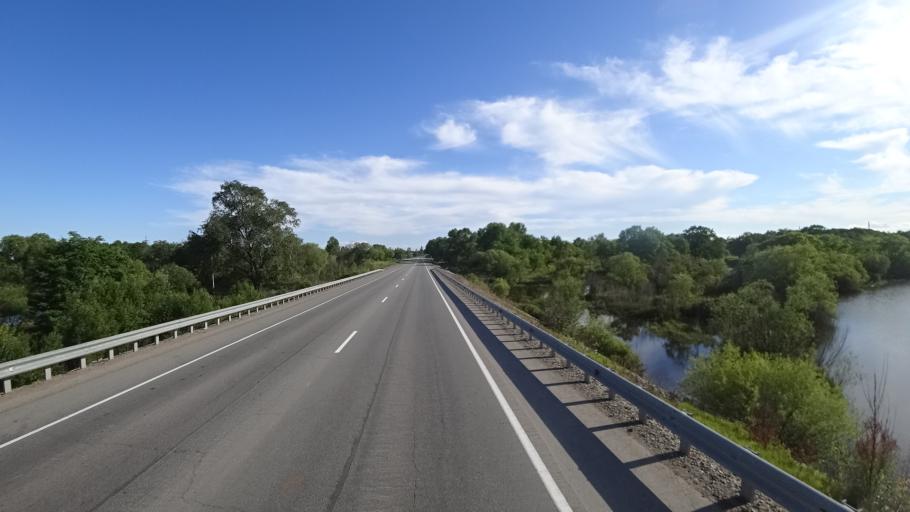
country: RU
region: Khabarovsk Krai
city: Khor
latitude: 47.8599
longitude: 134.9628
